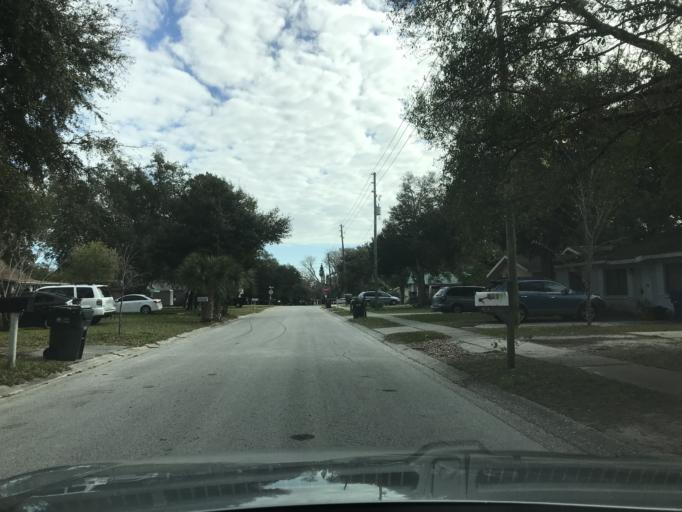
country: US
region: Florida
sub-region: Pinellas County
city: Largo
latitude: 27.9185
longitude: -82.7821
